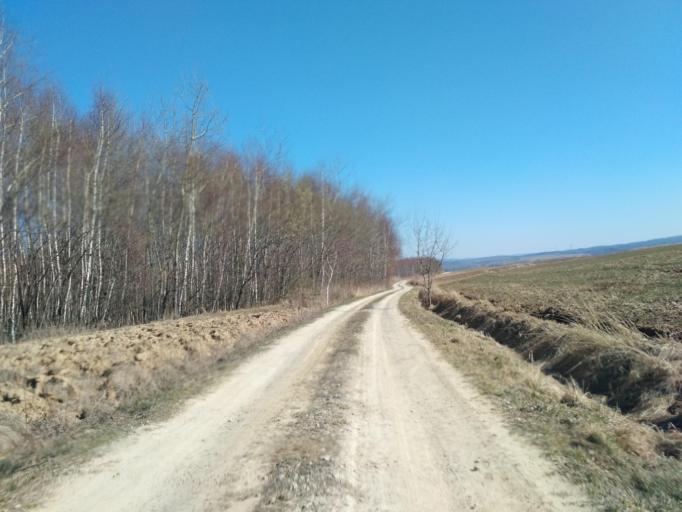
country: PL
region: Subcarpathian Voivodeship
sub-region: Powiat ropczycko-sedziszowski
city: Wielopole Skrzynskie
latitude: 49.9529
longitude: 21.5617
